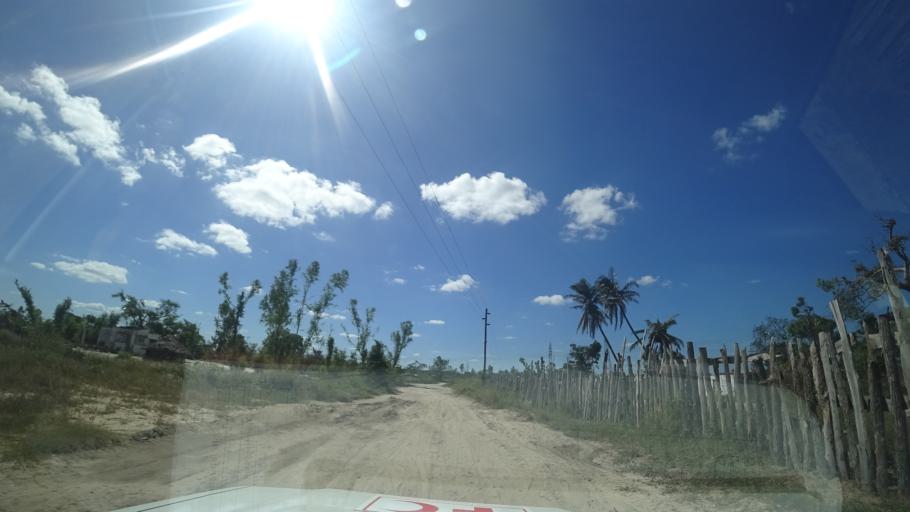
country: MZ
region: Sofala
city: Dondo
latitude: -19.5074
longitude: 34.6097
